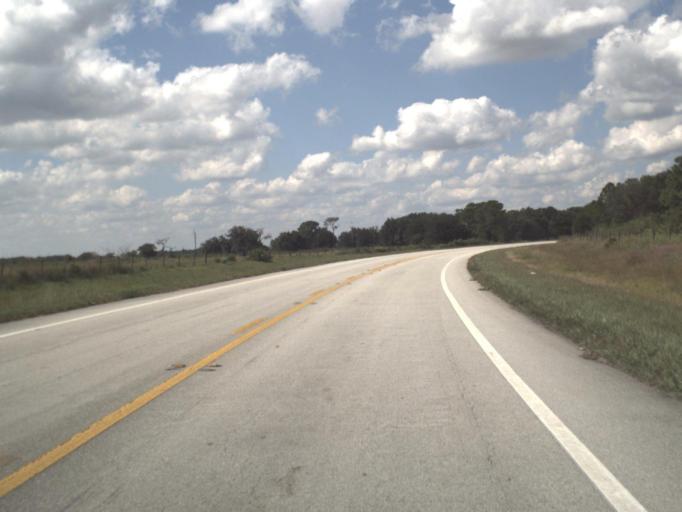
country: US
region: Florida
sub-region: Highlands County
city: Sebring
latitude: 27.4123
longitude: -81.5571
